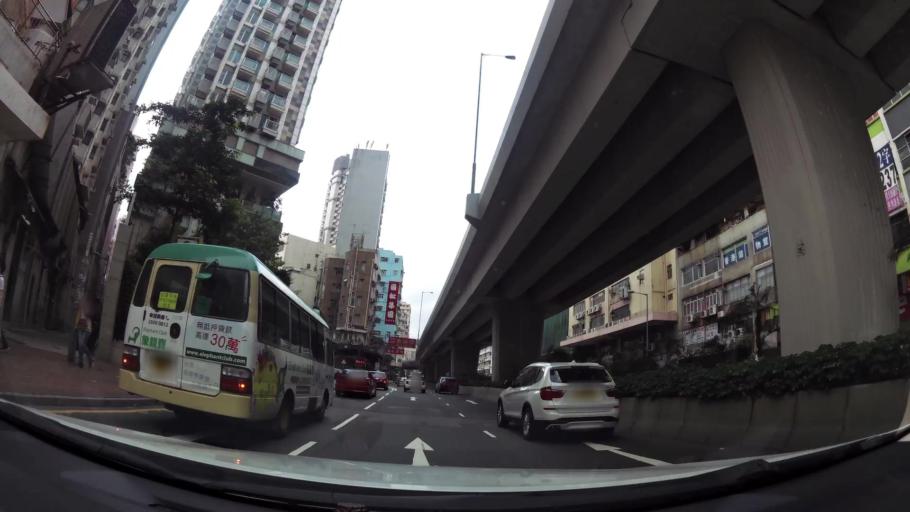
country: HK
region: Sham Shui Po
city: Sham Shui Po
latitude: 22.3205
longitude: 114.1655
